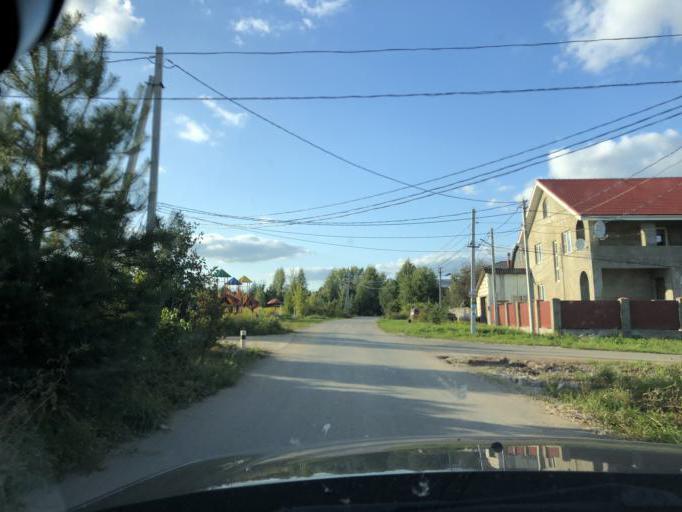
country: RU
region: Tula
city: Kosaya Gora
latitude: 54.1757
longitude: 37.5446
